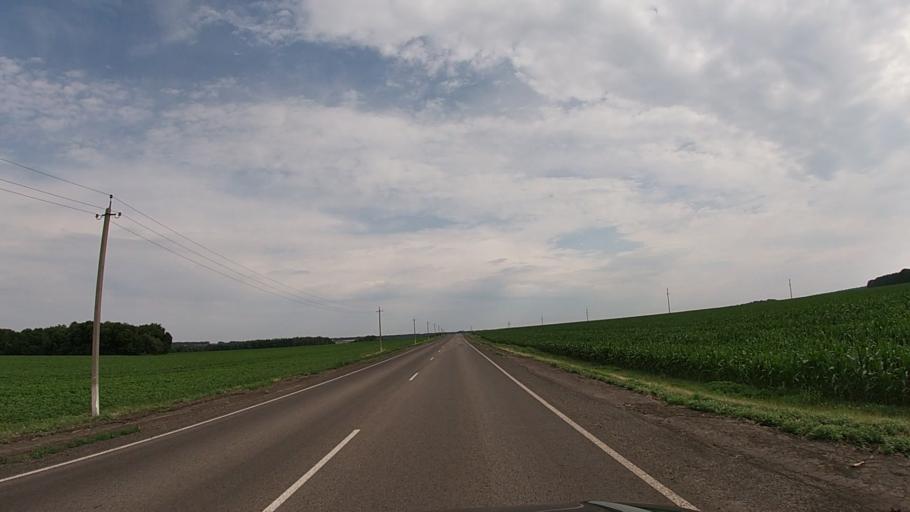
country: RU
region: Belgorod
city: Krasnaya Yaruga
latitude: 50.8155
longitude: 35.5018
